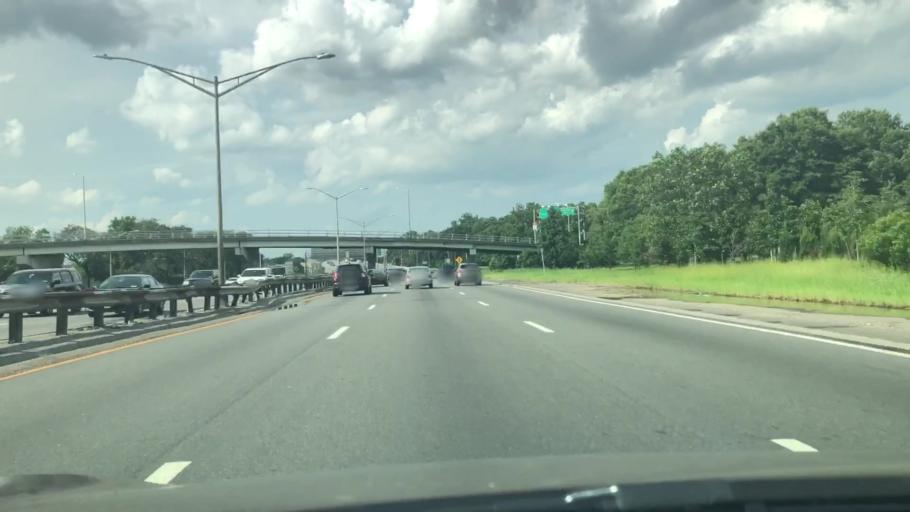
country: US
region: New York
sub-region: Queens County
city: Jamaica
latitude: 40.7359
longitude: -73.8364
